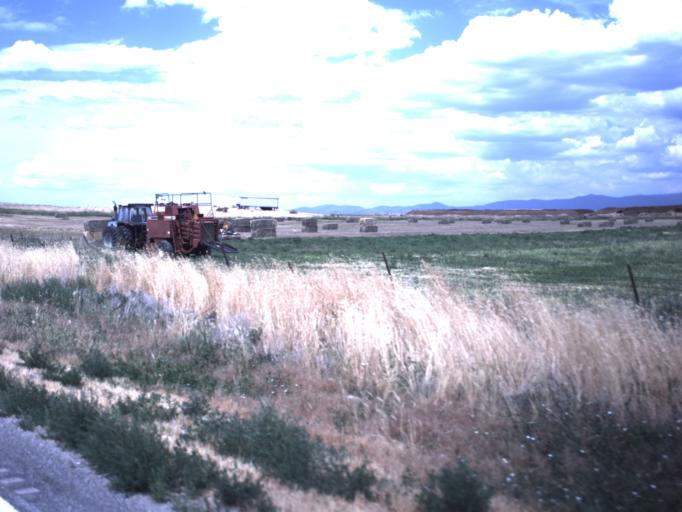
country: US
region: Utah
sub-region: Sanpete County
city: Moroni
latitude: 39.4918
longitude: -111.5631
